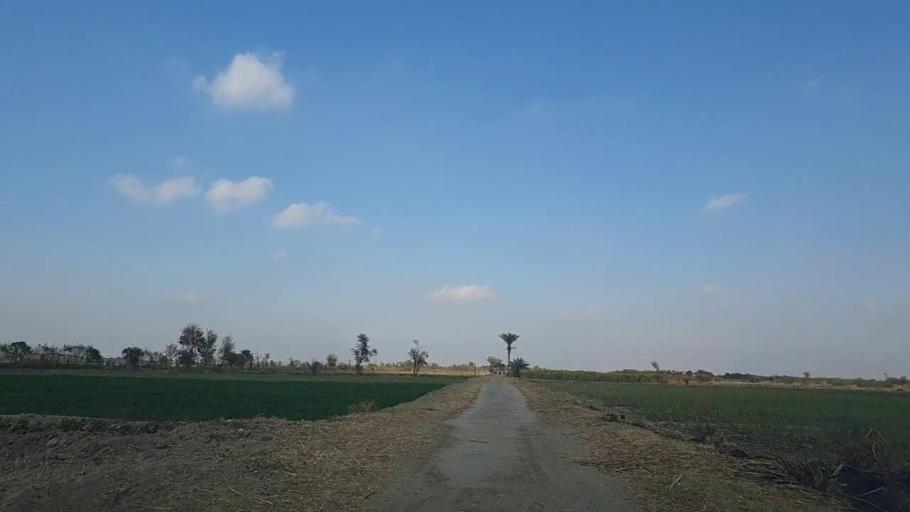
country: PK
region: Sindh
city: Tando Mittha Khan
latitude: 25.9957
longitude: 69.2504
